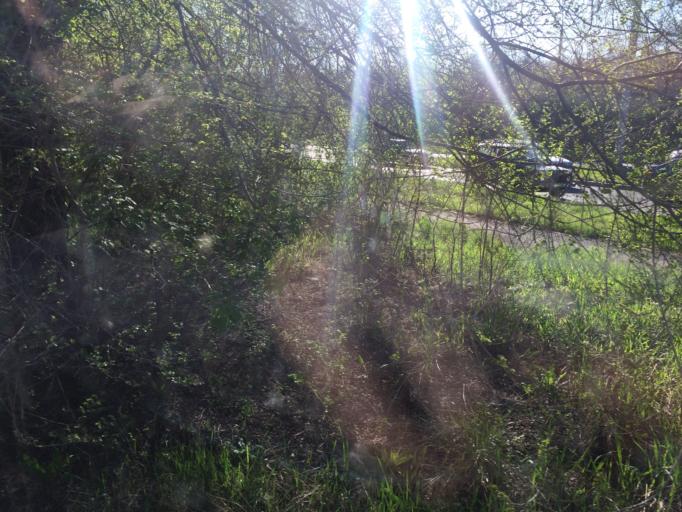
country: RU
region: Chelyabinsk
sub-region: Gorod Magnitogorsk
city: Magnitogorsk
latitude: 53.4007
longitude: 59.0408
